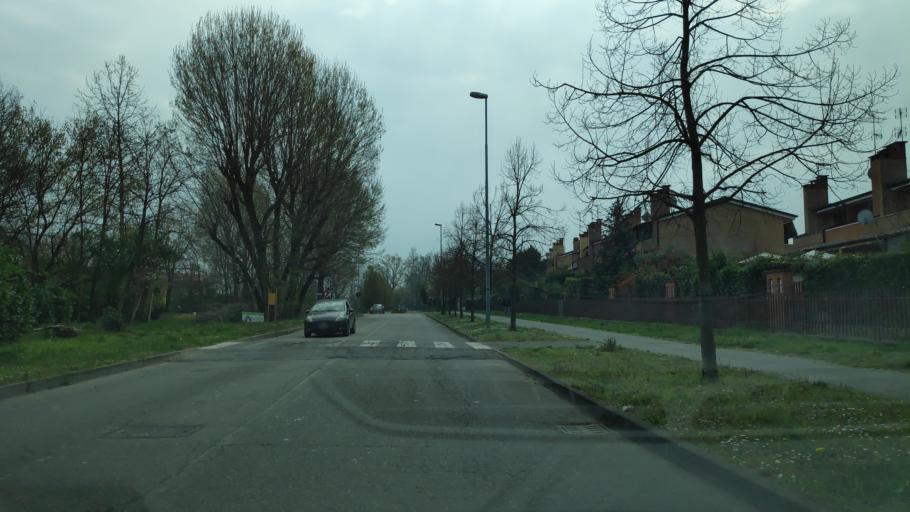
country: IT
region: Lombardy
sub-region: Citta metropolitana di Milano
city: Liscate
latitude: 45.4798
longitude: 9.4152
